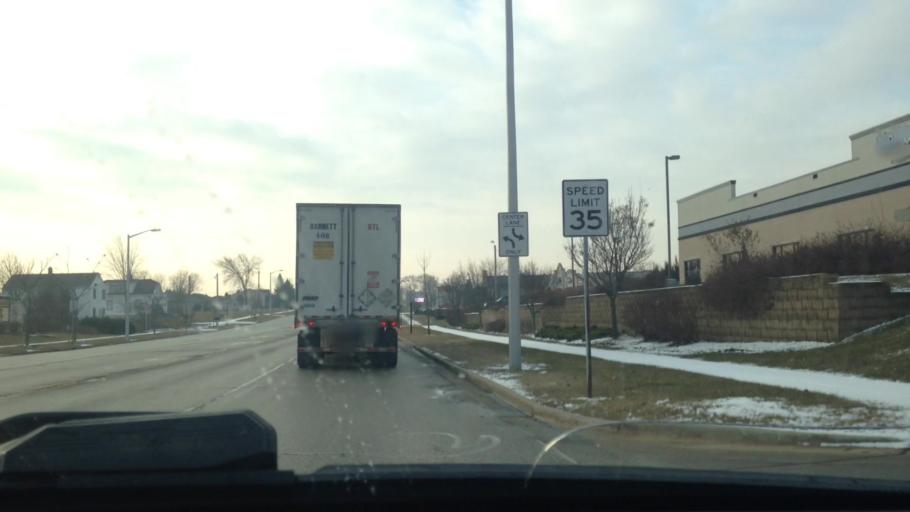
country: US
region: Wisconsin
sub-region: Washington County
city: West Bend
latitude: 43.3968
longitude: -88.1811
